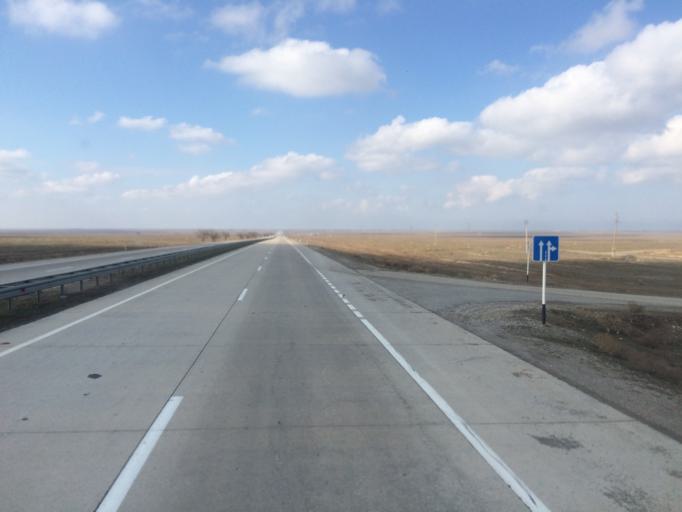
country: KZ
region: Ongtustik Qazaqstan
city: Temirlanovka
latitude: 42.8288
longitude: 69.1319
